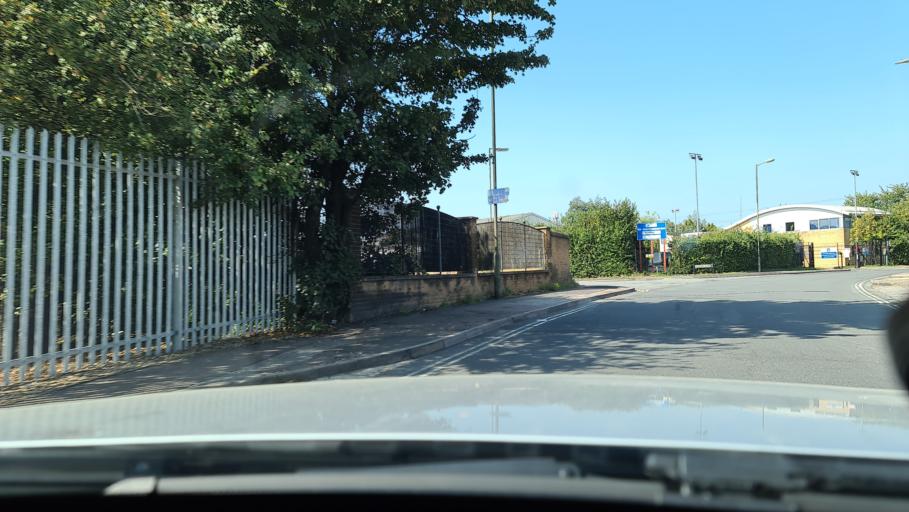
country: GB
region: England
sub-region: Oxfordshire
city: Banbury
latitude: 52.0729
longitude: -1.3246
